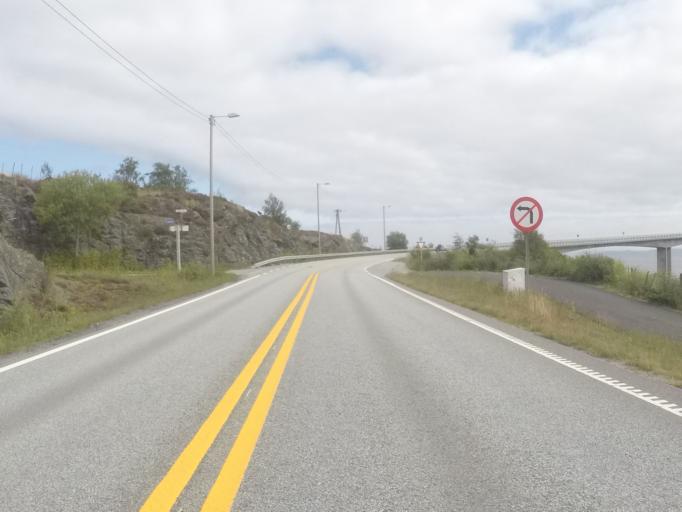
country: NO
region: Rogaland
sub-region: Bokn
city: Bokn
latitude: 59.2542
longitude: 5.4696
